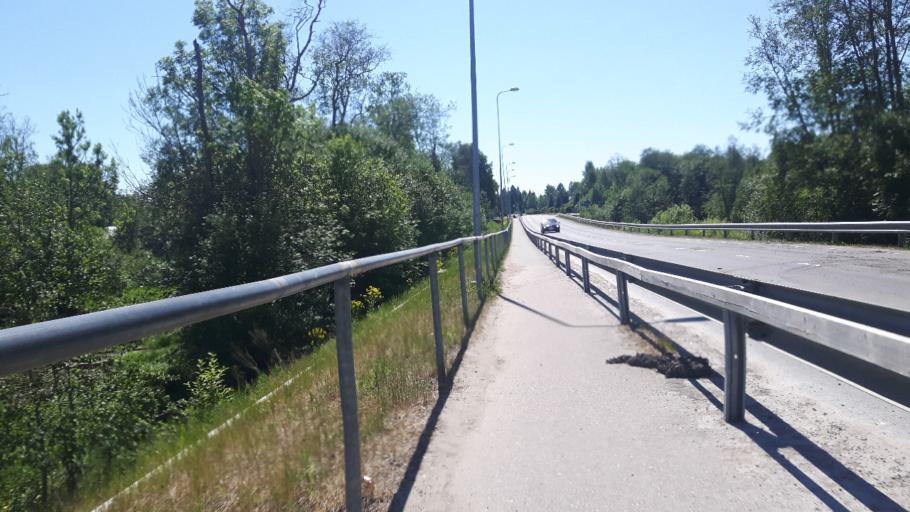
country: EE
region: Harju
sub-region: Saku vald
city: Saku
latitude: 59.2337
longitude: 24.6820
